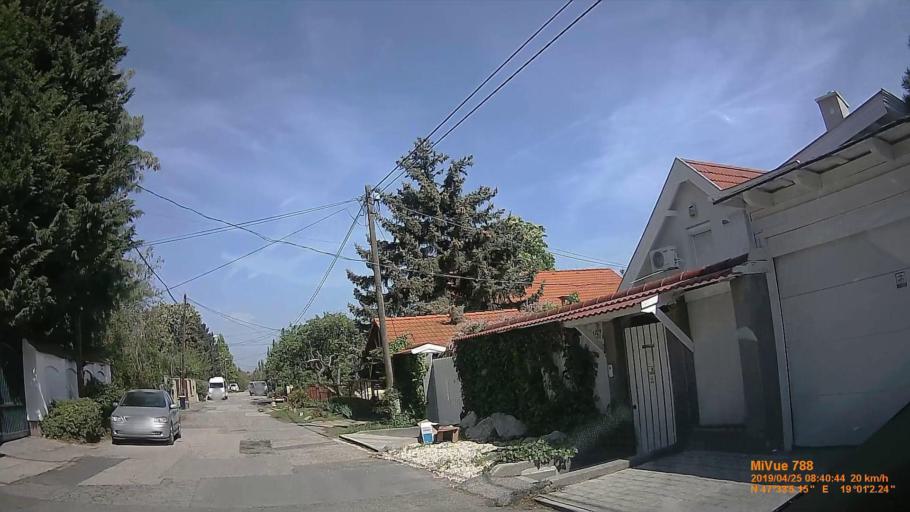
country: HU
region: Budapest
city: Budapest III. keruelet
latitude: 47.5514
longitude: 19.0172
